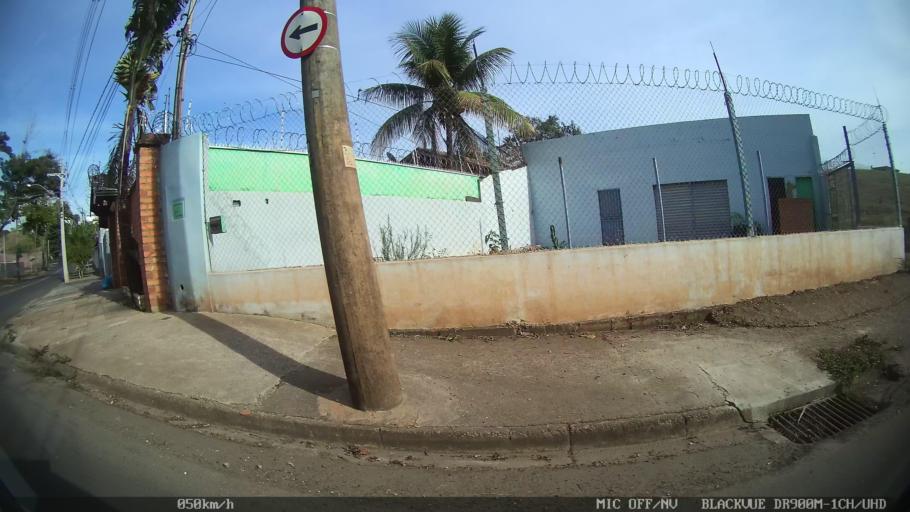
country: BR
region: Sao Paulo
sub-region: Piracicaba
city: Piracicaba
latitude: -22.7079
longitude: -47.6777
